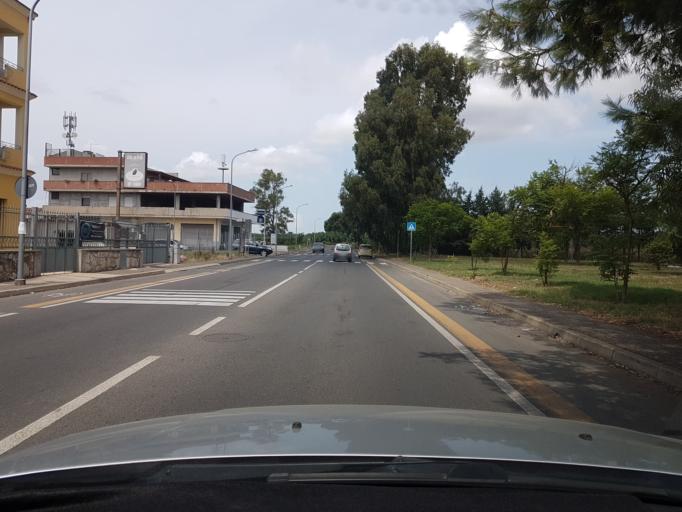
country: IT
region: Sardinia
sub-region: Provincia di Oristano
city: Oristano
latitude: 39.9143
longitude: 8.5891
